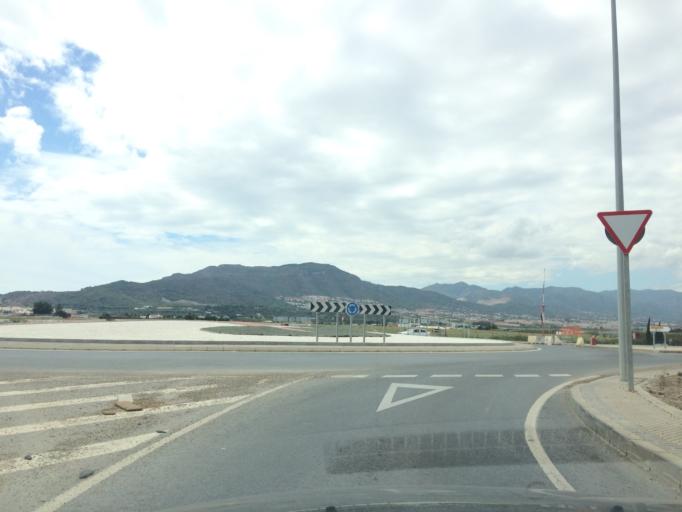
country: ES
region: Andalusia
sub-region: Provincia de Malaga
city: Alhaurin de la Torre
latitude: 36.6879
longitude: -4.5113
